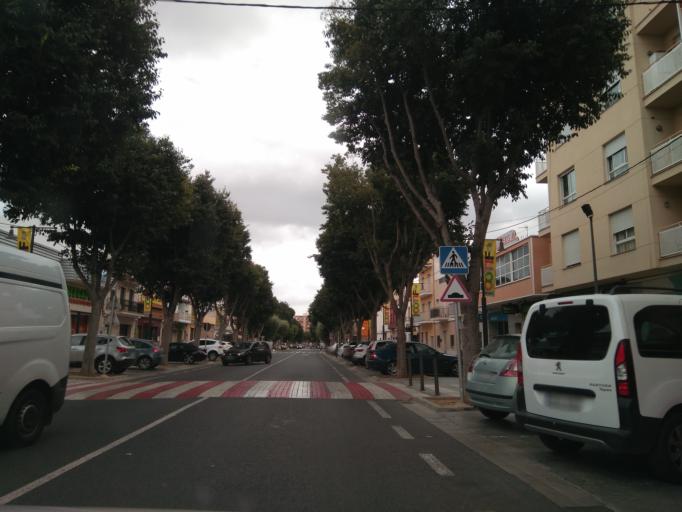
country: ES
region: Valencia
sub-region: Provincia de Valencia
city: L'Alcudia
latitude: 39.1986
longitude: -0.5044
